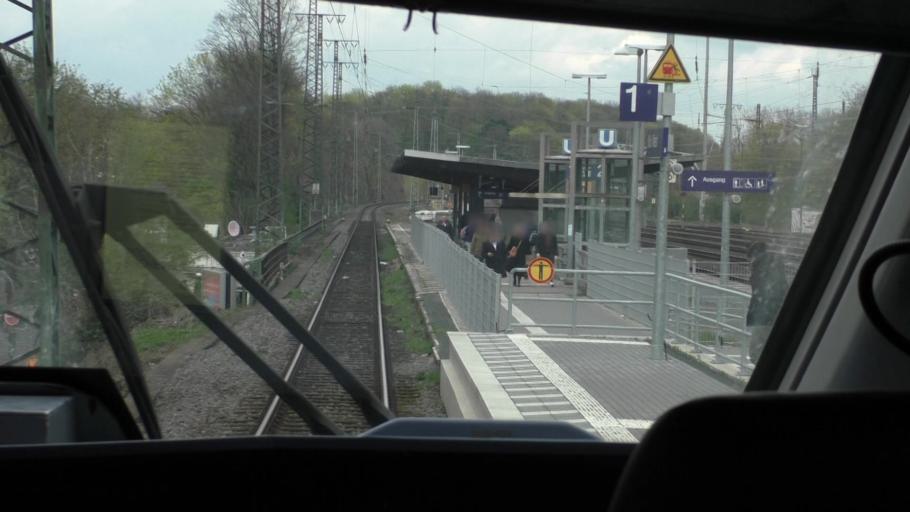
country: DE
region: North Rhine-Westphalia
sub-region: Regierungsbezirk Koln
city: Neuehrenfeld
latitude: 50.9425
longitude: 6.9331
